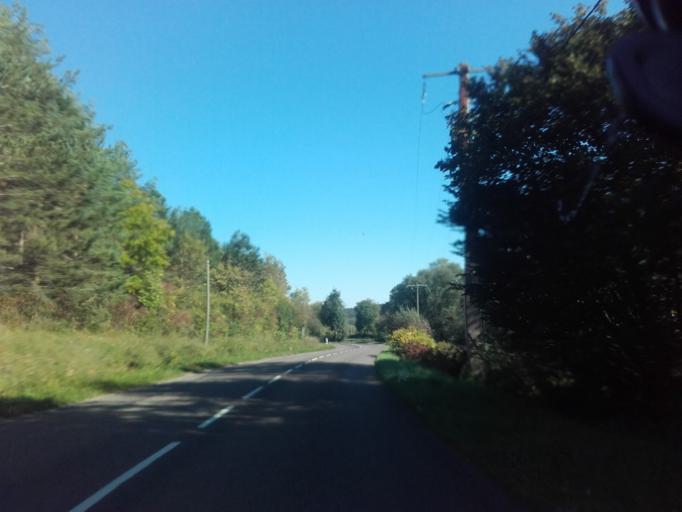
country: FR
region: Bourgogne
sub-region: Departement de la Cote-d'Or
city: Meursault
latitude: 47.0193
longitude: 4.7575
